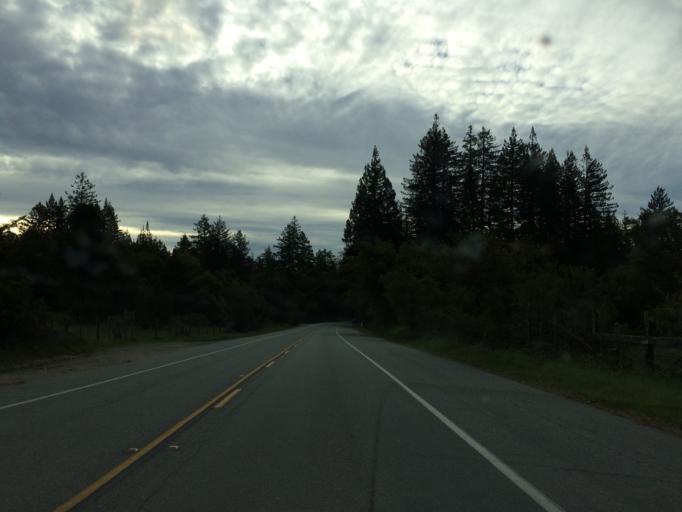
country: US
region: California
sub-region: Santa Cruz County
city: Felton
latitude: 37.0221
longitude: -122.0859
